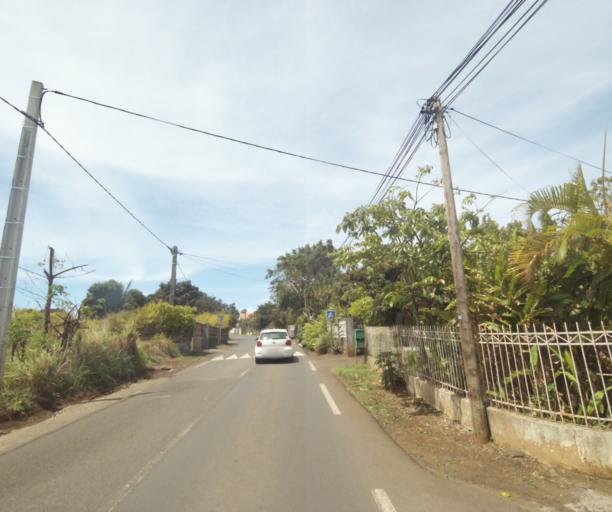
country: RE
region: Reunion
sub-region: Reunion
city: Saint-Paul
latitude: -21.0472
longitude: 55.2789
